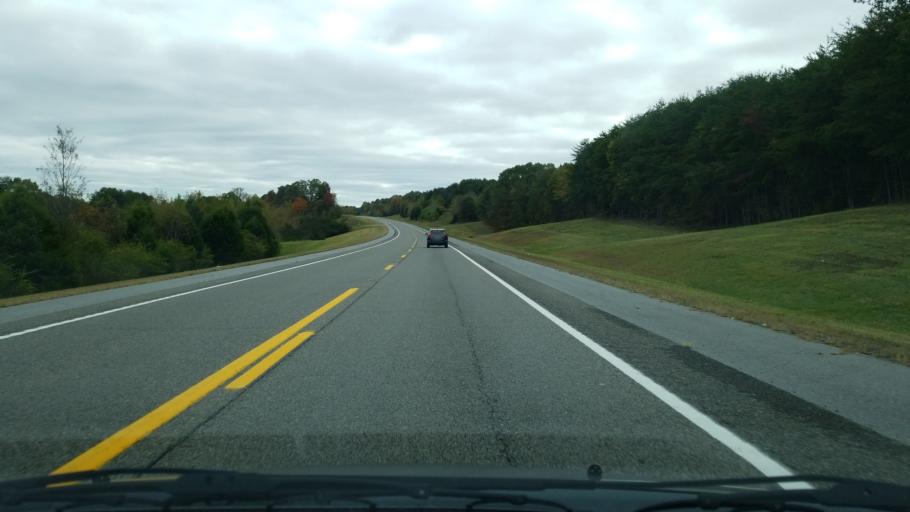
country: US
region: Tennessee
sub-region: Rhea County
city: Graysville
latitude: 35.4297
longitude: -85.0251
